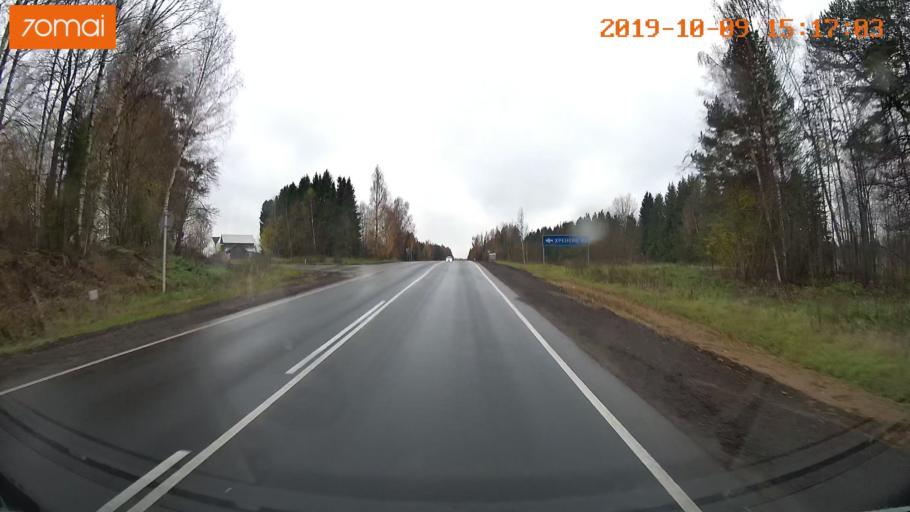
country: RU
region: Kostroma
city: Susanino
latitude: 58.1035
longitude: 41.5841
